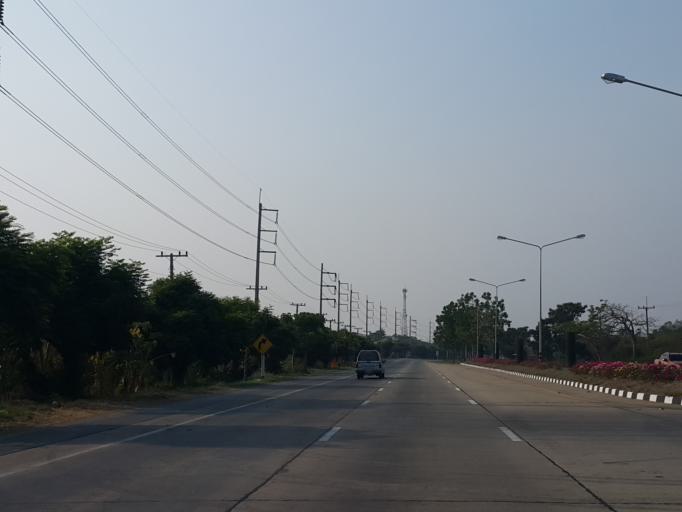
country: TH
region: Suphan Buri
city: Doem Bang Nang Buat
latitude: 14.9303
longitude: 100.0840
